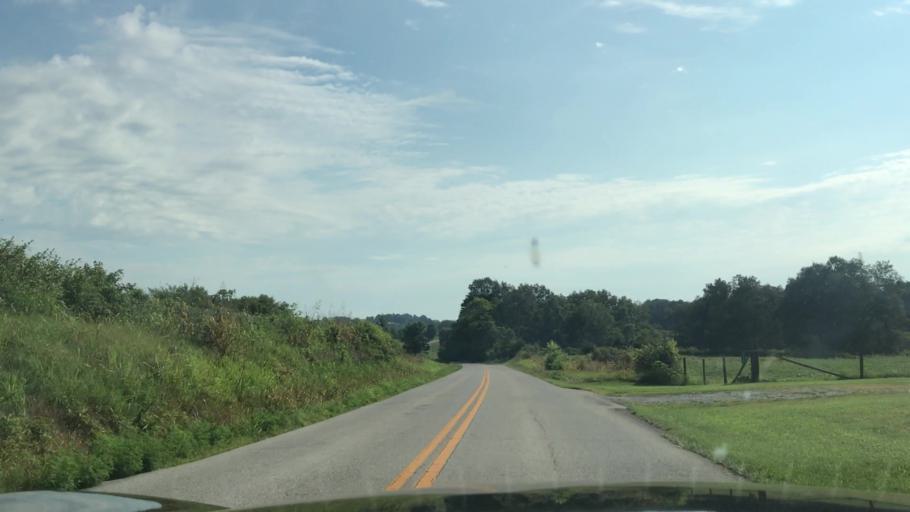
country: US
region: Kentucky
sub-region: Hart County
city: Munfordville
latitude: 37.2222
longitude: -85.7238
